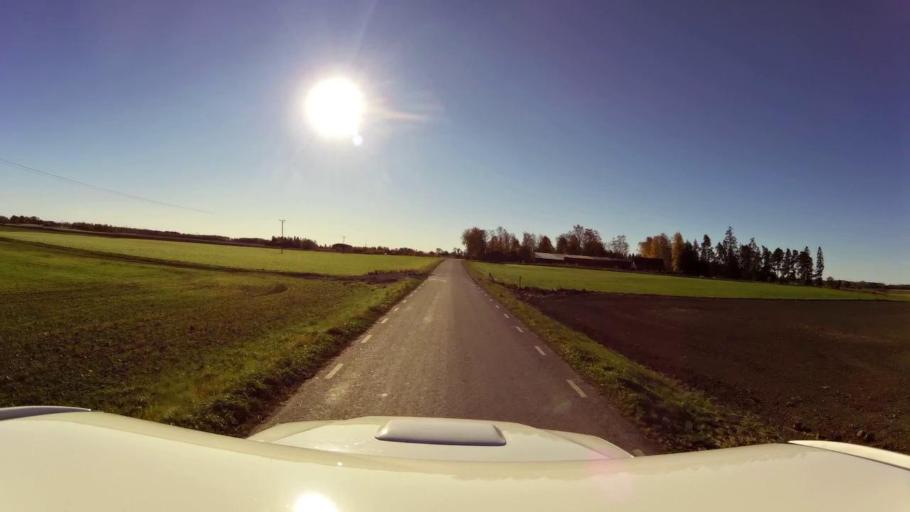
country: SE
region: OEstergoetland
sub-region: Linkopings Kommun
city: Ljungsbro
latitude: 58.5027
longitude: 15.4184
